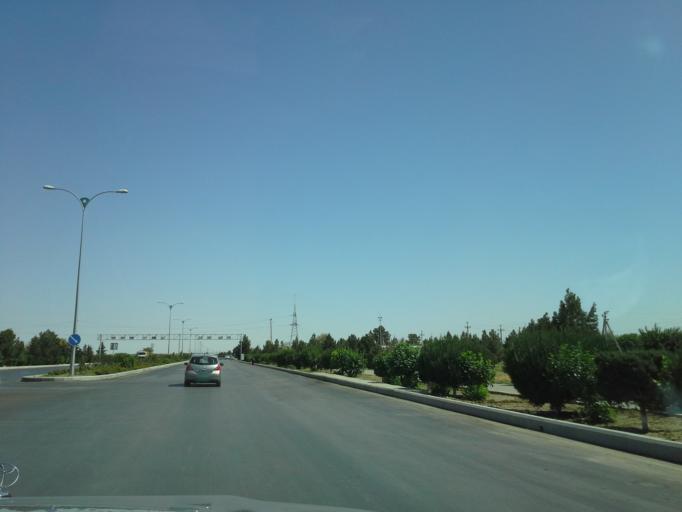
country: TM
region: Ahal
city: Annau
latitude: 37.9171
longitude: 58.4649
